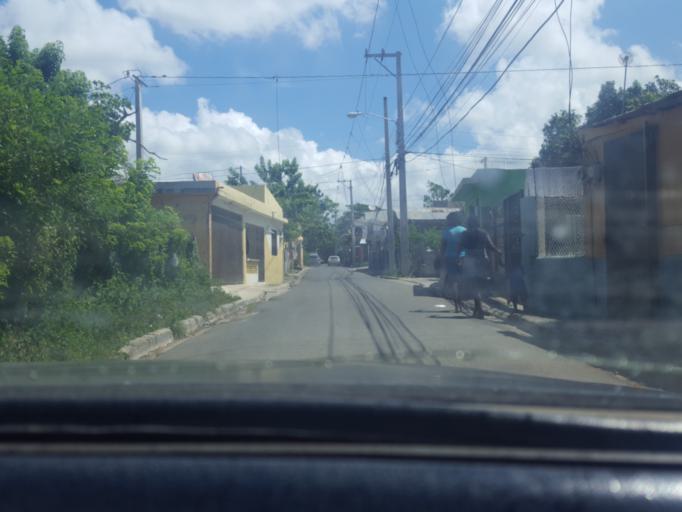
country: DO
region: Santiago
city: Santiago de los Caballeros
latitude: 19.4892
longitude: -70.6961
